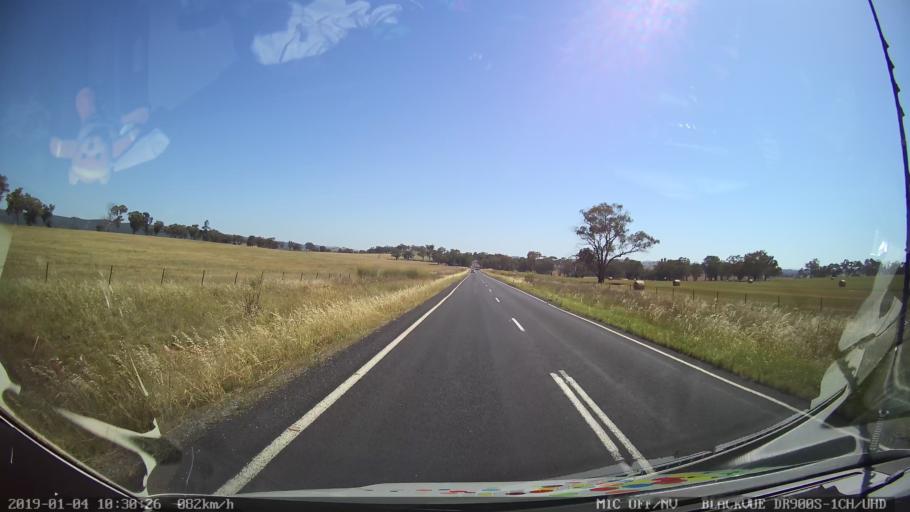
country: AU
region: New South Wales
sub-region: Cabonne
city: Canowindra
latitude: -33.3458
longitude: 148.6278
